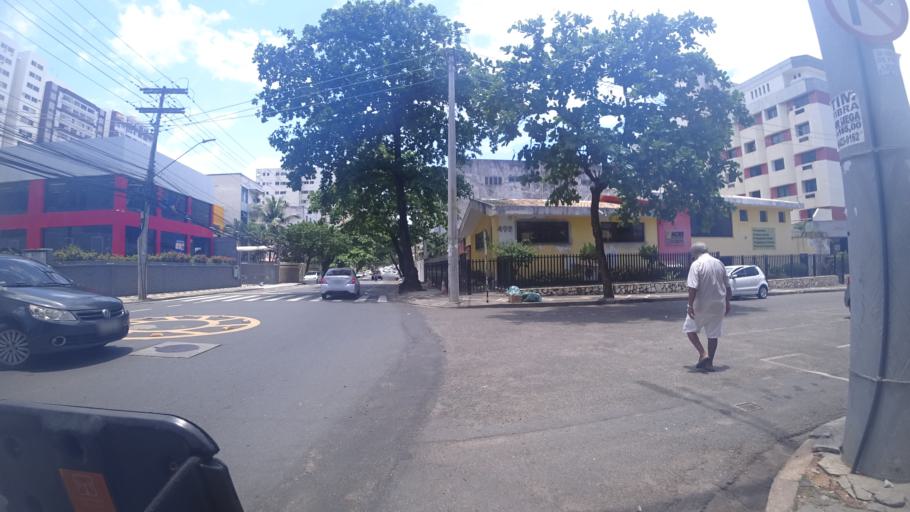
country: BR
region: Bahia
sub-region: Salvador
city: Salvador
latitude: -13.0064
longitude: -38.4629
